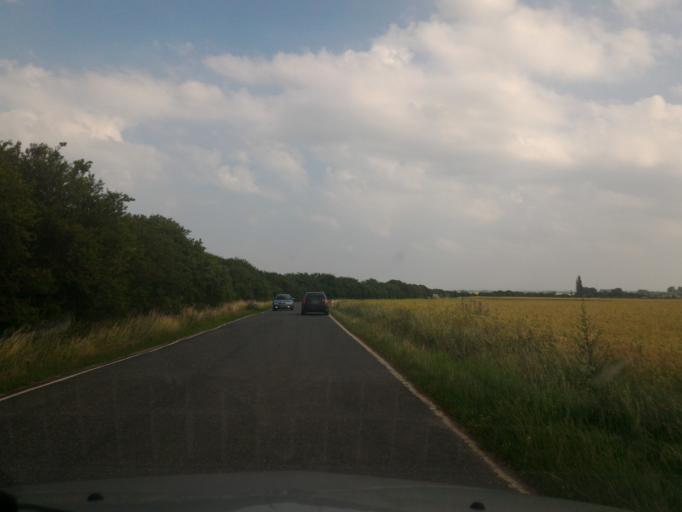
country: CZ
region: Central Bohemia
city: Loucen
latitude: 50.2619
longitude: 15.0231
